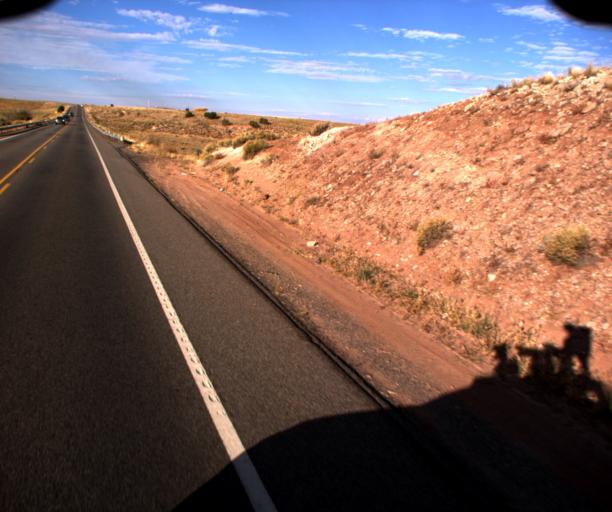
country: US
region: New Mexico
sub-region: San Juan County
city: Shiprock
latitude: 36.9279
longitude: -109.1650
